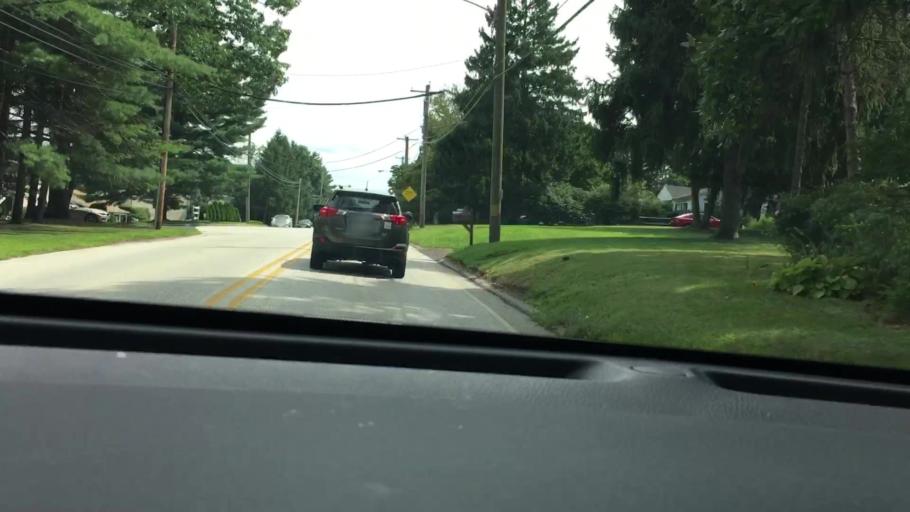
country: US
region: Pennsylvania
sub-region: Bucks County
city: Warminster Heights
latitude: 40.1640
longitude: -75.0832
